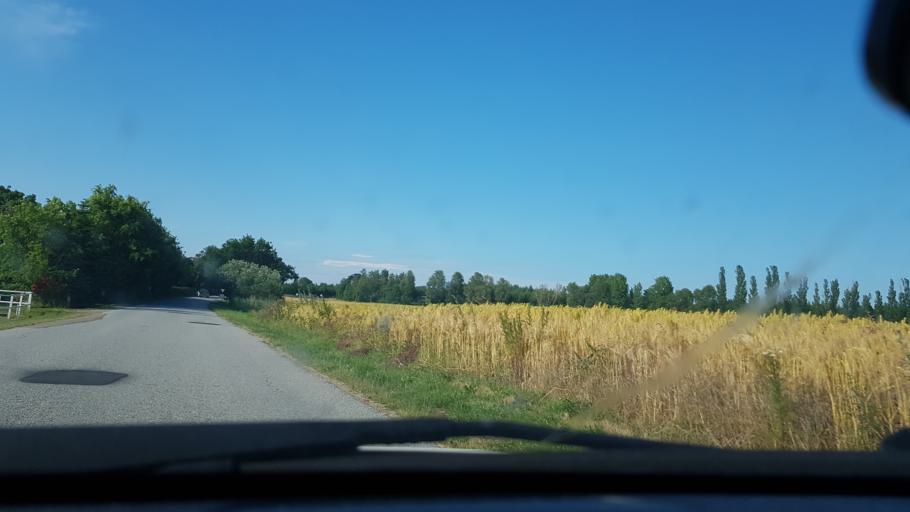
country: DK
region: Zealand
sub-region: Odsherred Kommune
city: Hojby
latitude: 55.8952
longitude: 11.6157
